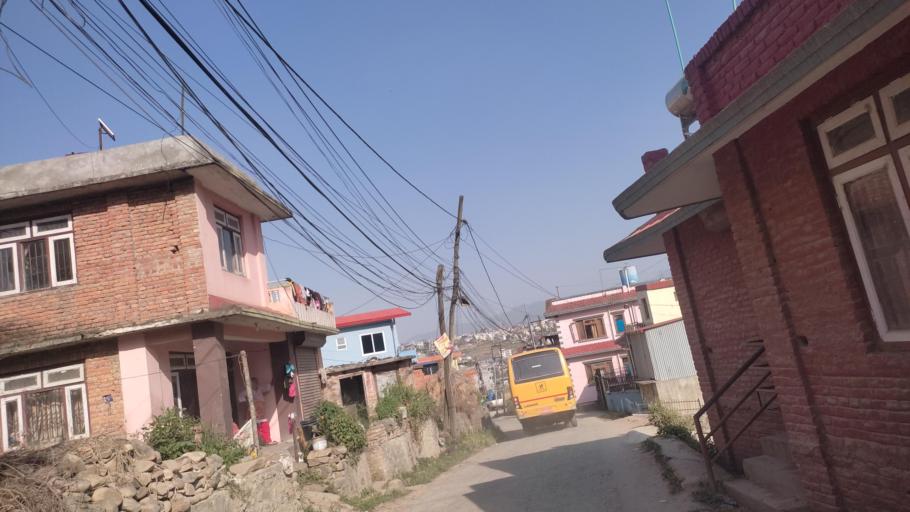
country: NP
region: Central Region
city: Kirtipur
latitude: 27.6541
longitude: 85.2838
